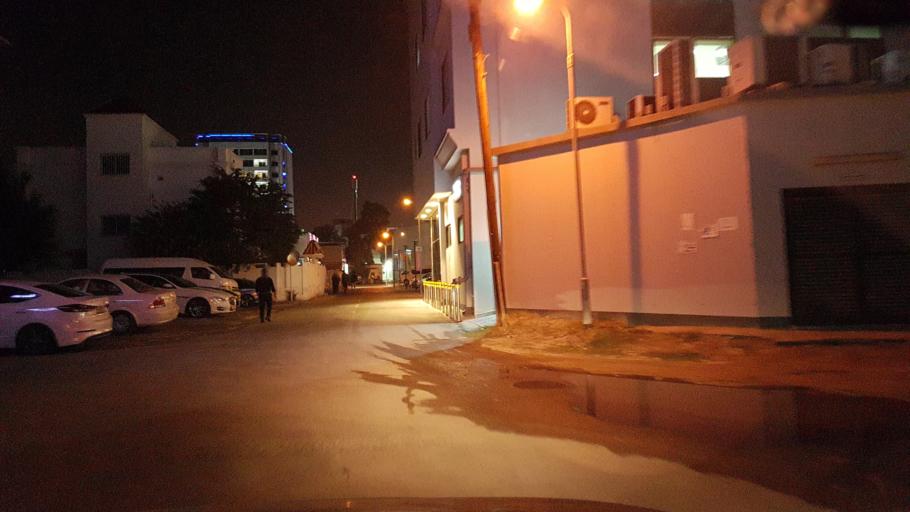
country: BH
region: Manama
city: Manama
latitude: 26.2187
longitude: 50.5855
